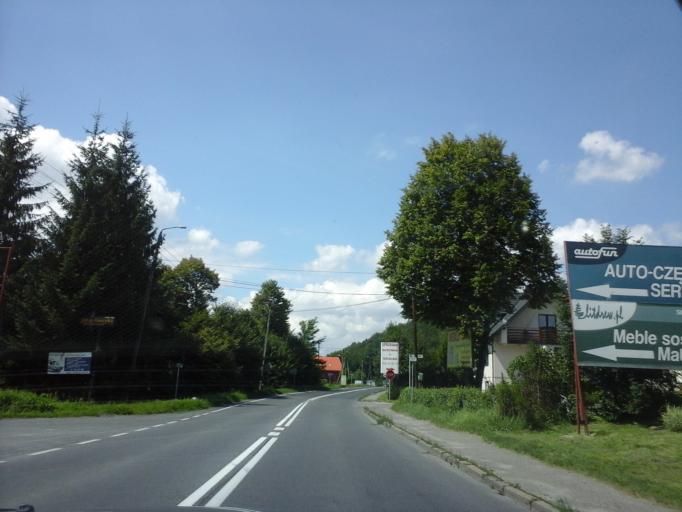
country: PL
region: Lesser Poland Voivodeship
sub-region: Powiat suski
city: Makow Podhalanski
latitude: 49.7315
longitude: 19.6632
